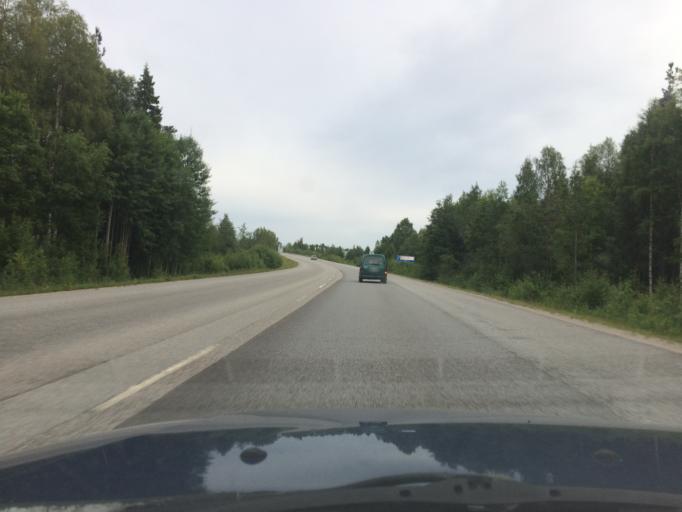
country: SE
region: Norrbotten
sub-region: Pitea Kommun
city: Pitea
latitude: 65.3278
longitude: 21.4296
